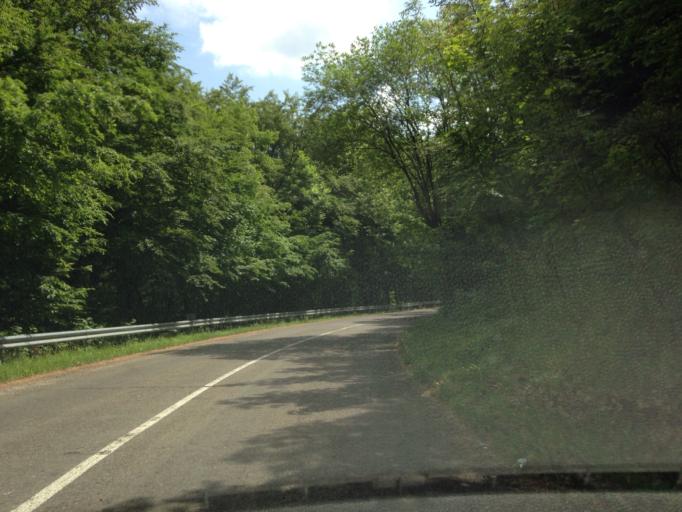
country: HU
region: Pest
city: Visegrad
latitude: 47.7289
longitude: 18.9552
